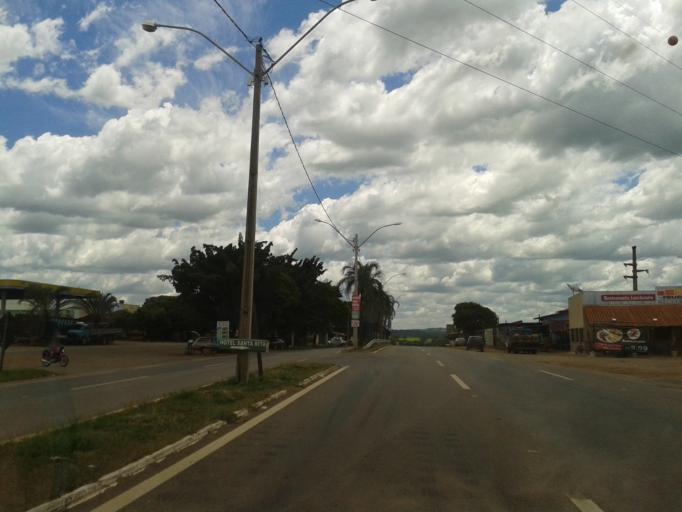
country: BR
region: Goias
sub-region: Petrolina De Goias
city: Petrolina de Goias
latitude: -16.1070
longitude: -49.3346
